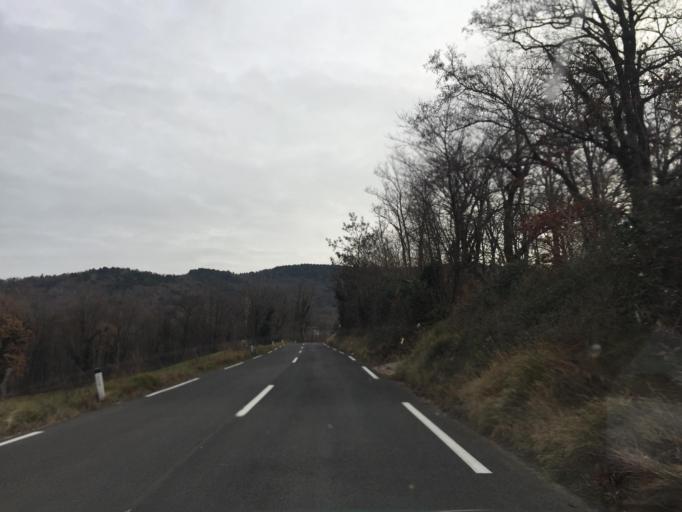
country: SI
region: Nova Gorica
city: Kromberk
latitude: 45.9849
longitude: 13.6922
